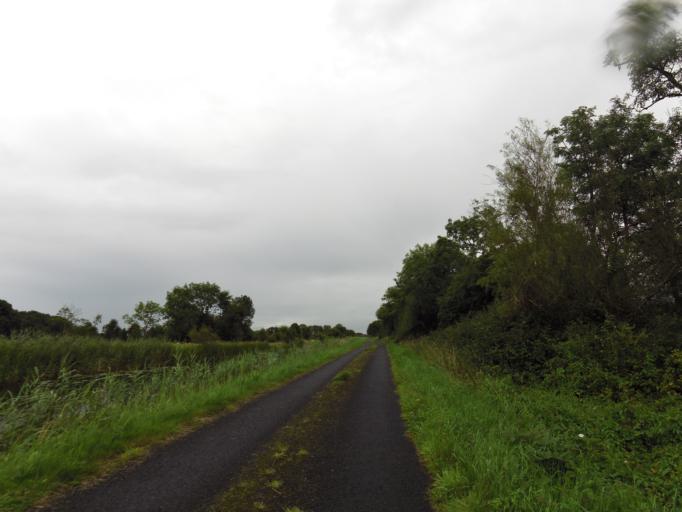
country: IE
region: Leinster
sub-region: An Longfort
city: Edgeworthstown
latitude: 53.5806
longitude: -7.5782
